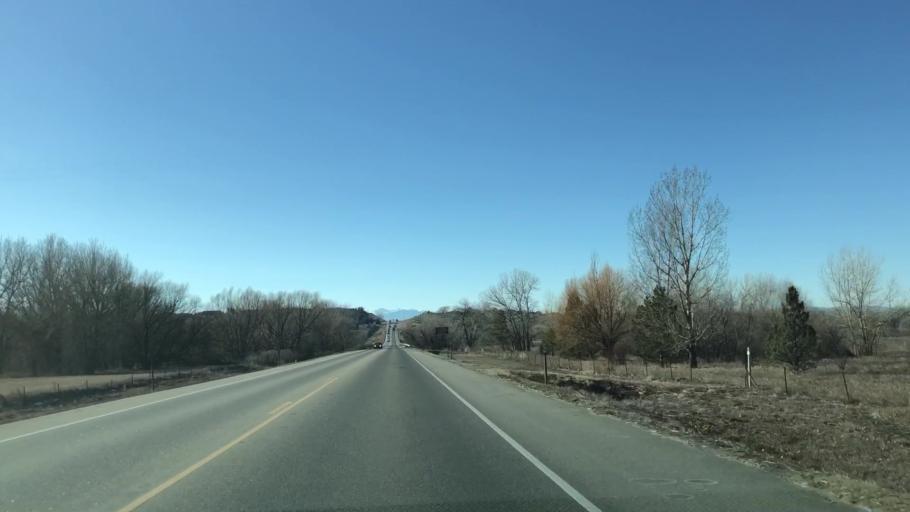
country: US
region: Colorado
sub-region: Weld County
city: Windsor
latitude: 40.4796
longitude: -104.9513
